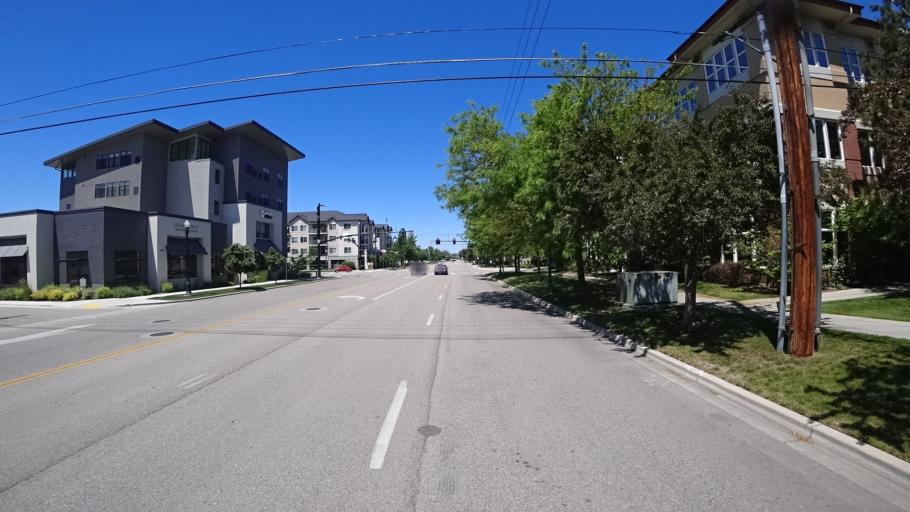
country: US
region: Idaho
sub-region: Ada County
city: Boise
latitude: 43.6146
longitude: -116.2145
